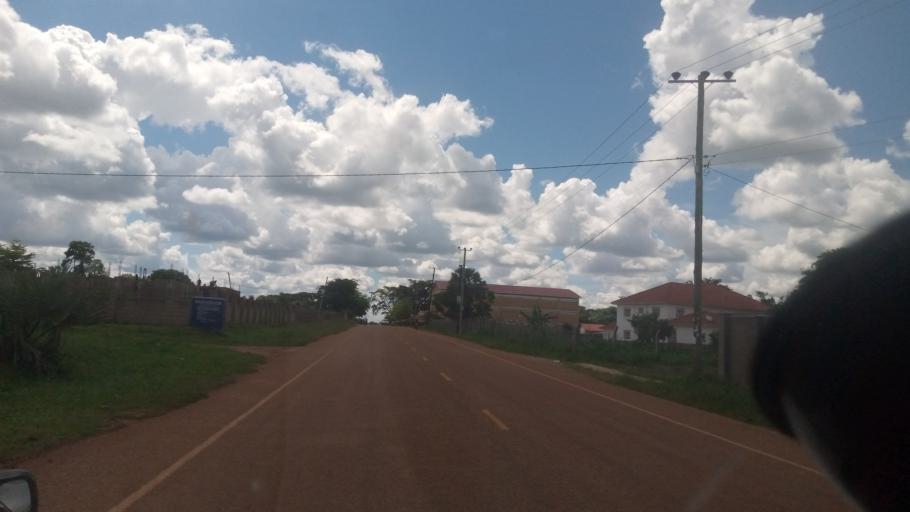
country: UG
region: Northern Region
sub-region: Lira District
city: Lira
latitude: 2.2418
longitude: 32.9082
